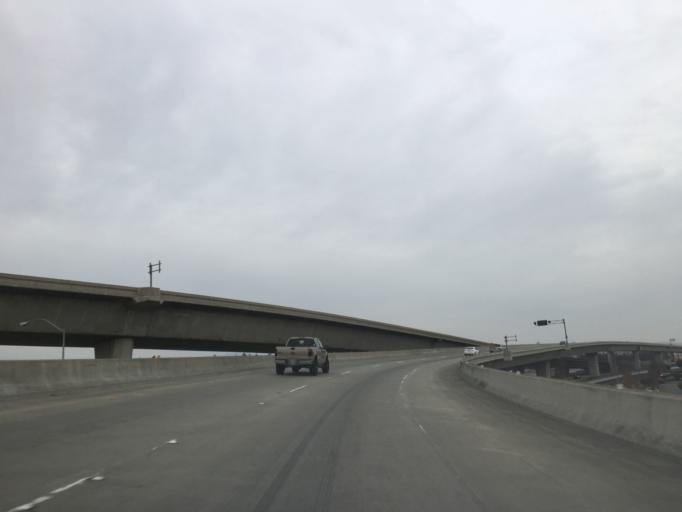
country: US
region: California
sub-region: Alameda County
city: Dublin
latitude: 37.7007
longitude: -121.9207
